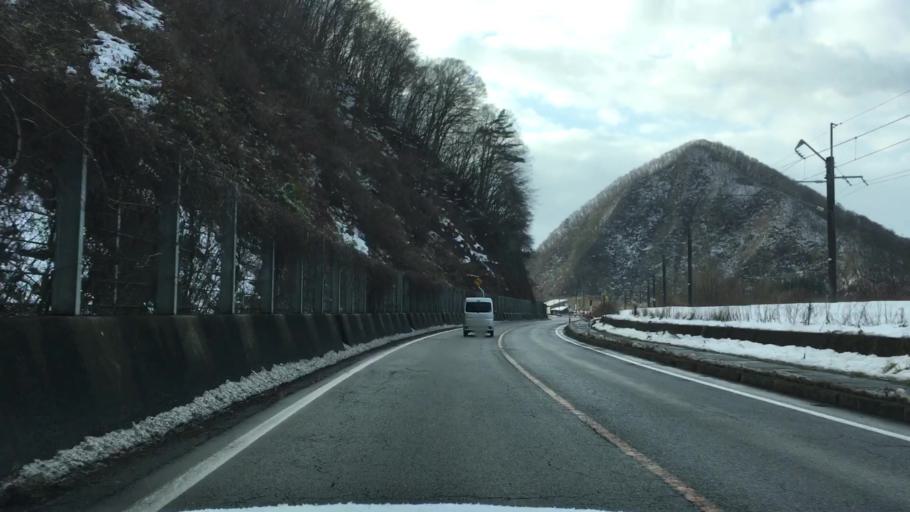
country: JP
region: Akita
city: Odate
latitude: 40.3642
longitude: 140.5976
